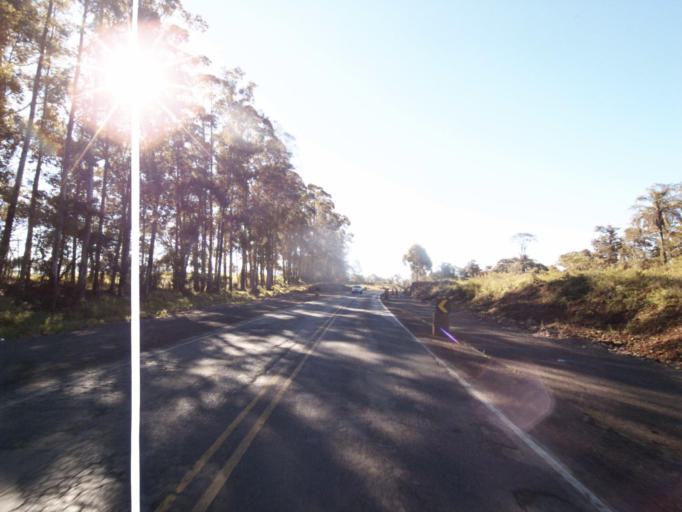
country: AR
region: Misiones
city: Bernardo de Irigoyen
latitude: -26.6712
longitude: -53.5195
